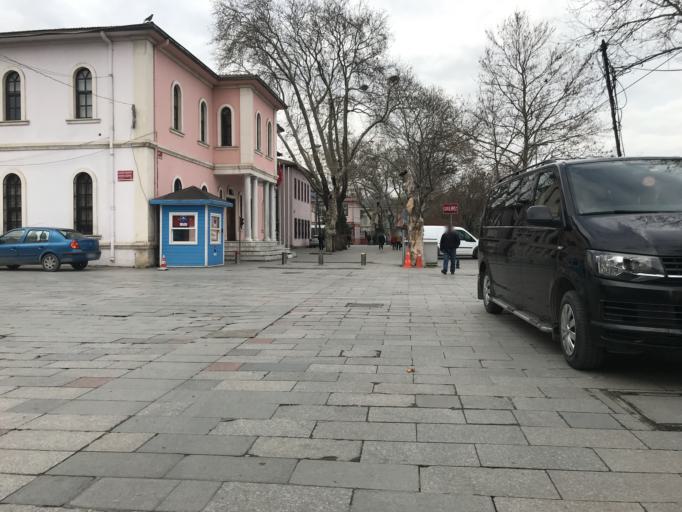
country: TR
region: Istanbul
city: Istanbul
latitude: 41.0430
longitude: 28.9372
